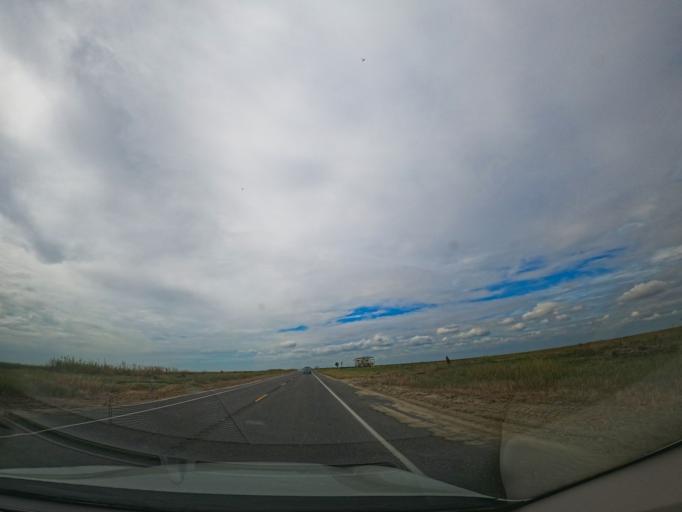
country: US
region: Louisiana
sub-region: Cameron Parish
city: Cameron
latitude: 29.7702
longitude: -93.4758
